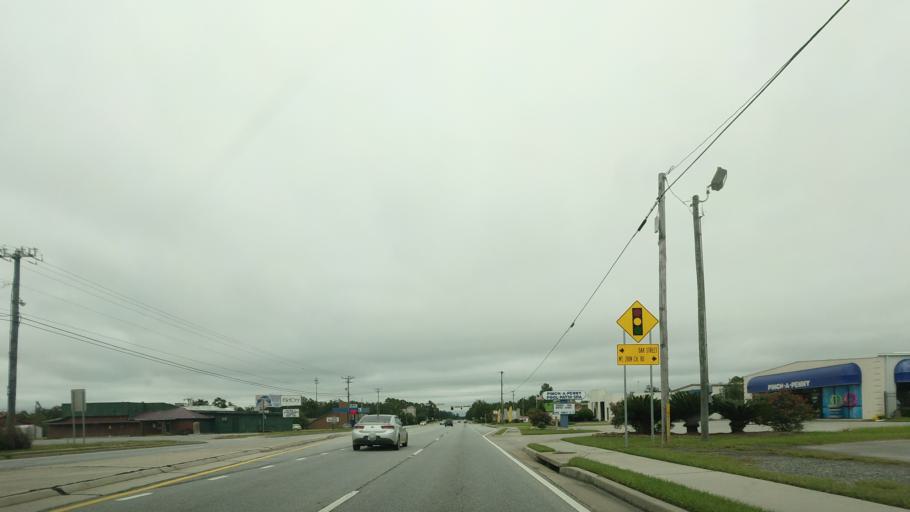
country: US
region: Georgia
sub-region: Lowndes County
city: Valdosta
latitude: 30.8885
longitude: -83.2712
